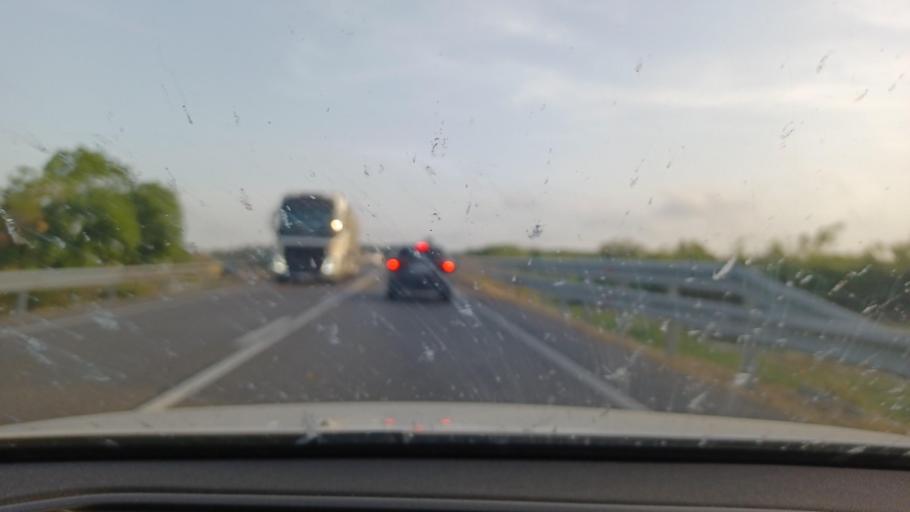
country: ES
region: Catalonia
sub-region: Provincia de Tarragona
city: Tortosa
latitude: 40.7941
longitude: 0.4973
